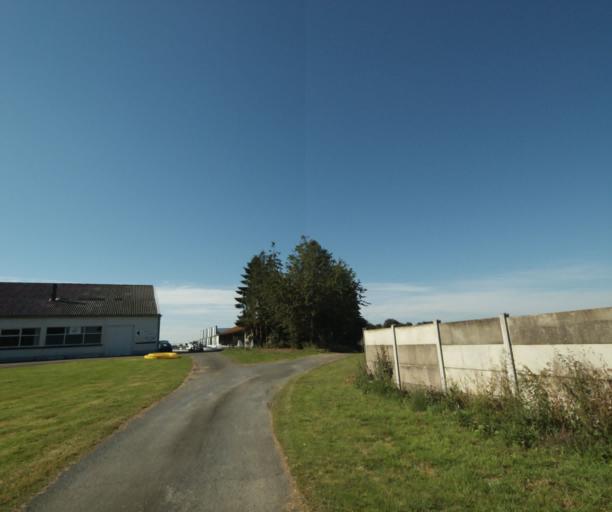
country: FR
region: Pays de la Loire
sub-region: Departement de la Mayenne
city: Laval
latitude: 48.0363
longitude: -0.7411
